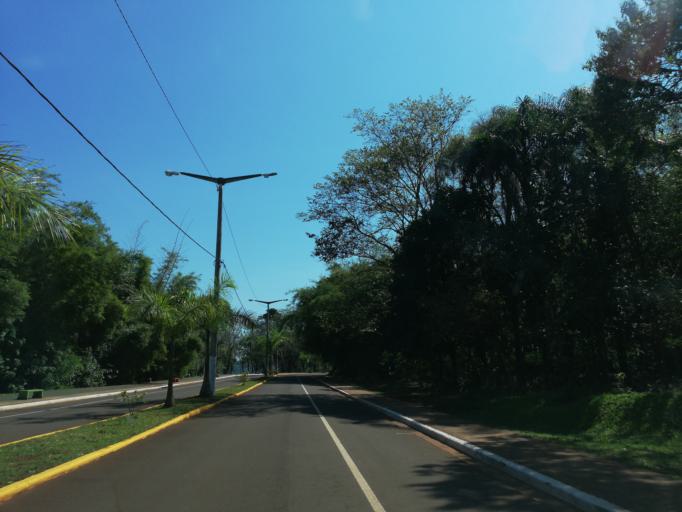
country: AR
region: Misiones
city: Puerto Eldorado
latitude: -26.4094
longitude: -54.6935
